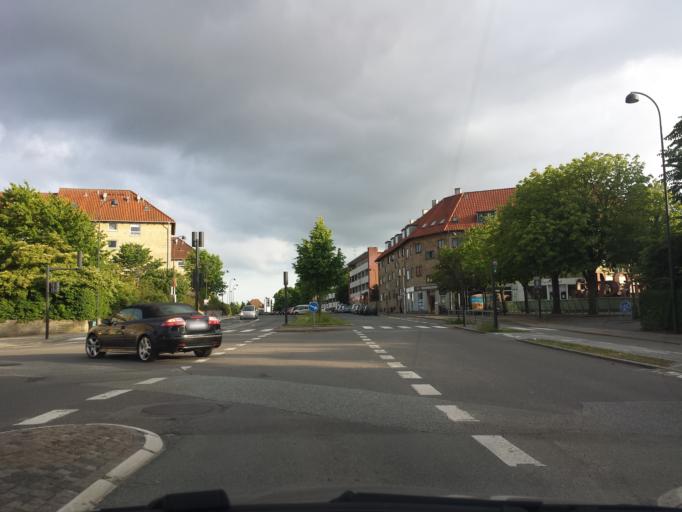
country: DK
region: Capital Region
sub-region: Lyngby-Tarbaek Kommune
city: Kongens Lyngby
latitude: 55.7523
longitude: 12.5194
